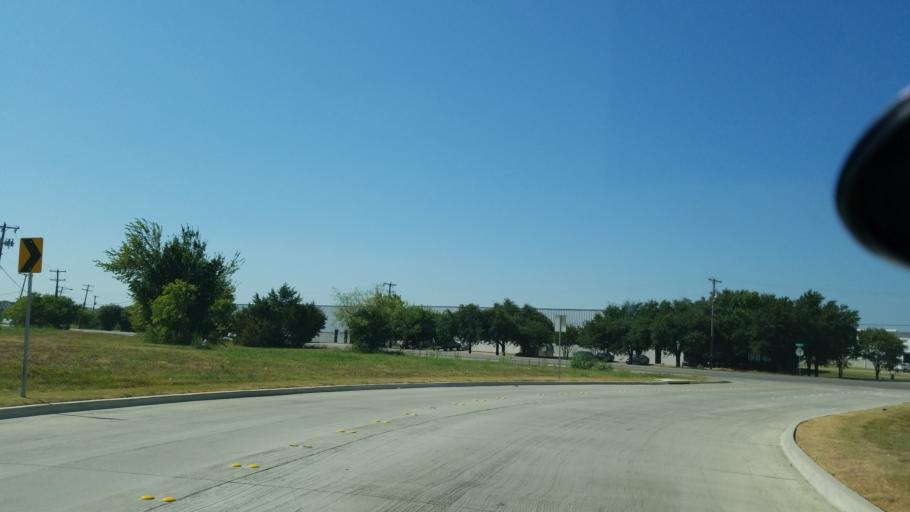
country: US
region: Texas
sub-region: Tarrant County
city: Mansfield
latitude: 32.5522
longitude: -97.1326
